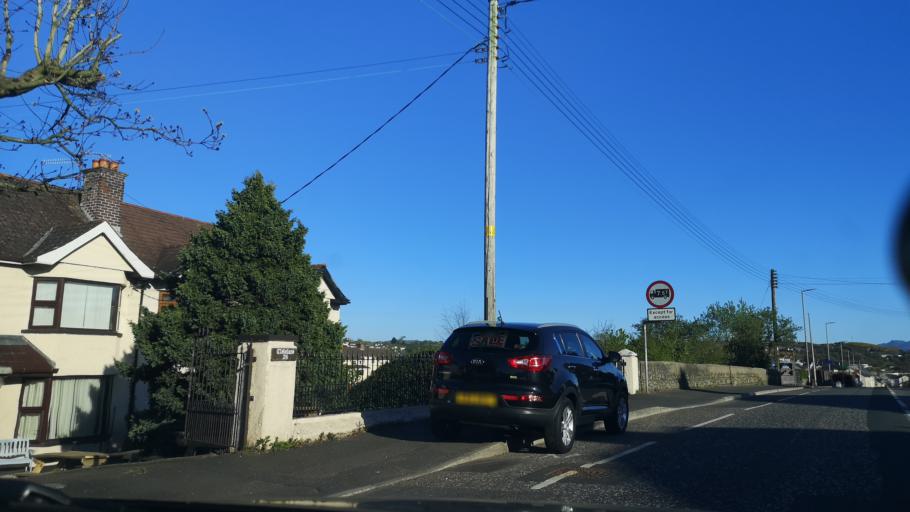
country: GB
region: Northern Ireland
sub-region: Newry and Mourne District
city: Newry
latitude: 54.1841
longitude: -6.3427
